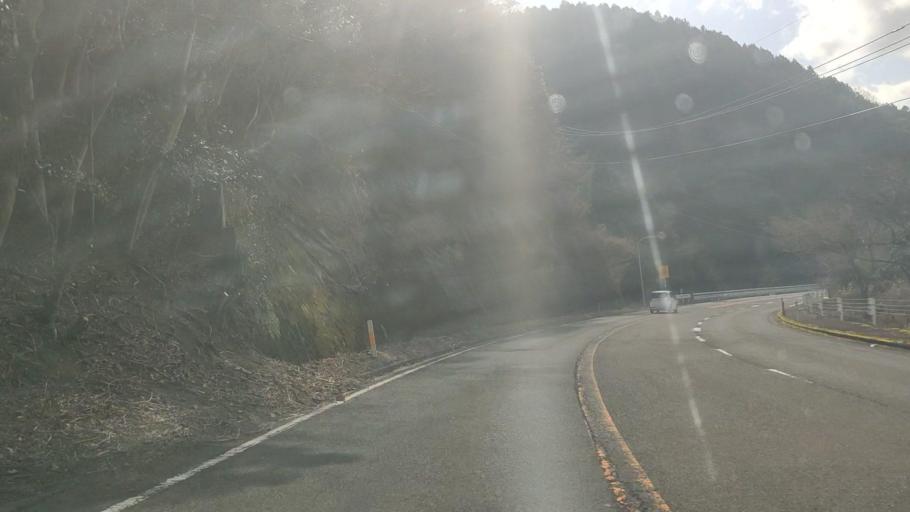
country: JP
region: Kumamoto
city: Hitoyoshi
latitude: 32.0782
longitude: 130.8033
